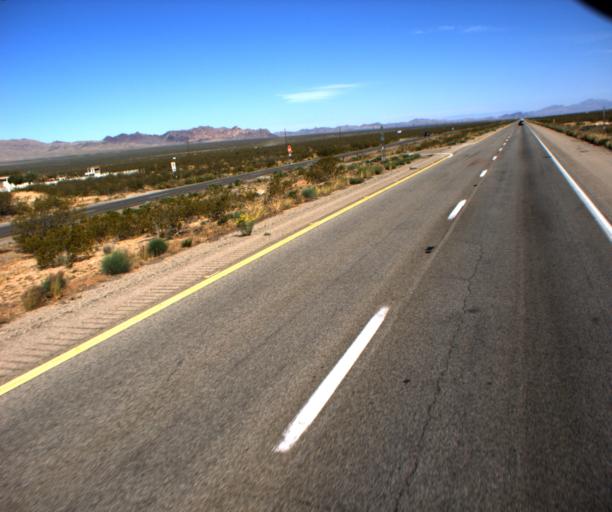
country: US
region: Arizona
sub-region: Mohave County
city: Dolan Springs
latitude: 35.5672
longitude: -114.3782
